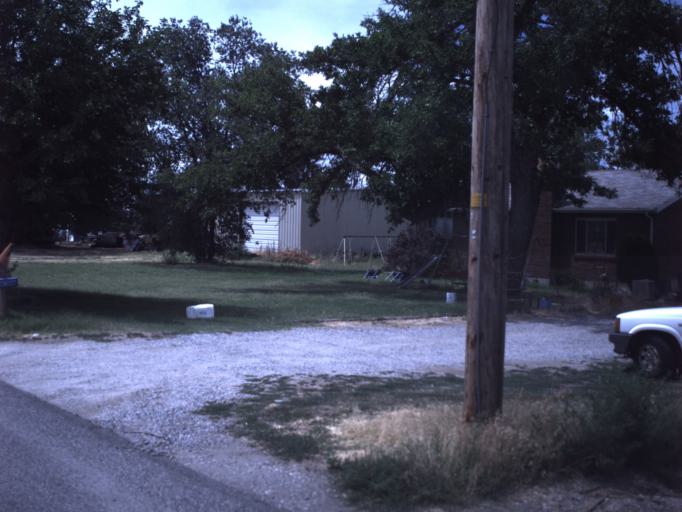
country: US
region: Utah
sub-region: Davis County
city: Clinton
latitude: 41.1263
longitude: -112.0646
